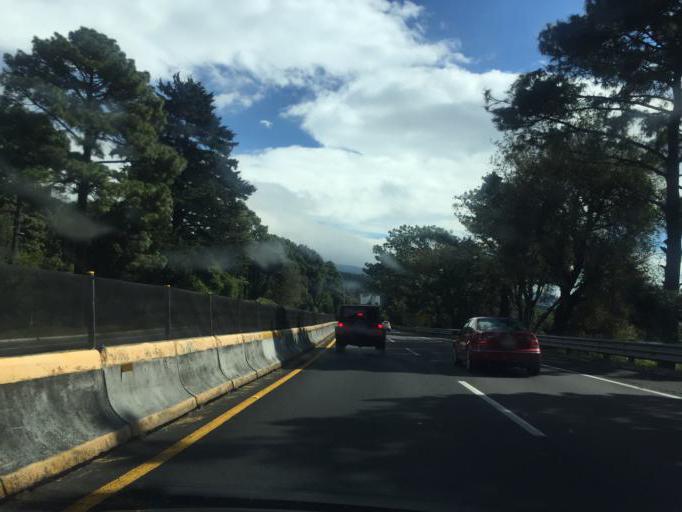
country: MX
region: Morelos
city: Tres Marias
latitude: 19.0309
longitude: -99.2123
